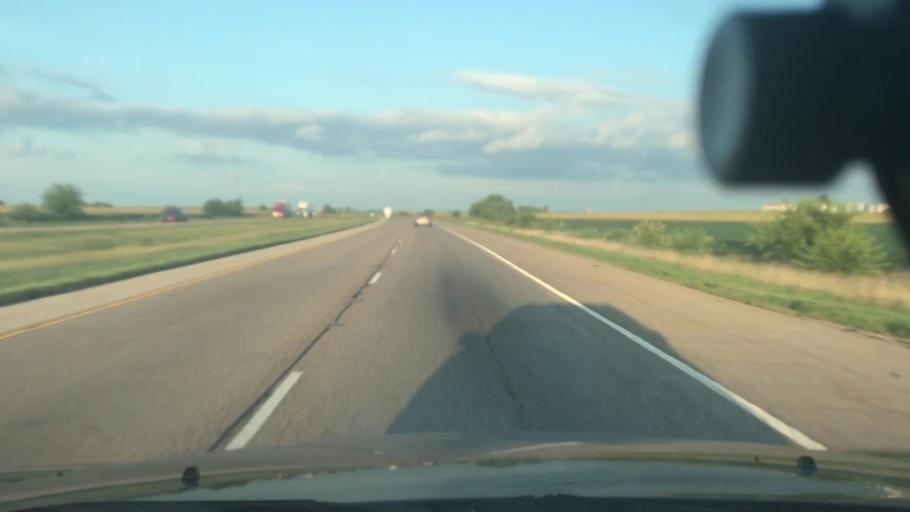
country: US
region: Illinois
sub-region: Clinton County
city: New Baden
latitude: 38.5173
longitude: -89.6994
